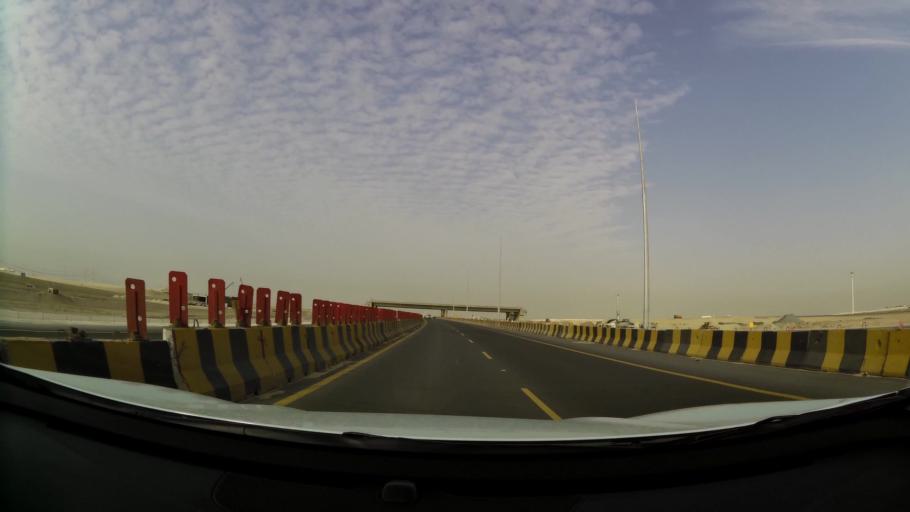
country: AE
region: Abu Dhabi
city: Abu Dhabi
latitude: 24.2446
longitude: 54.4708
